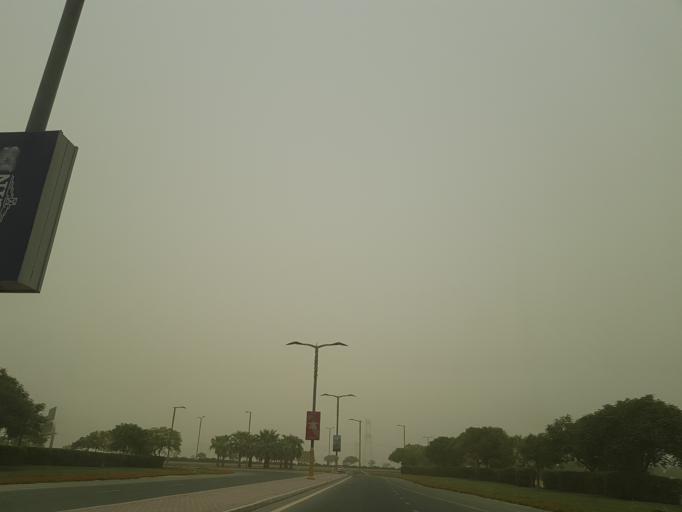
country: AE
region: Dubai
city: Dubai
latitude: 25.1635
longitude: 55.3011
